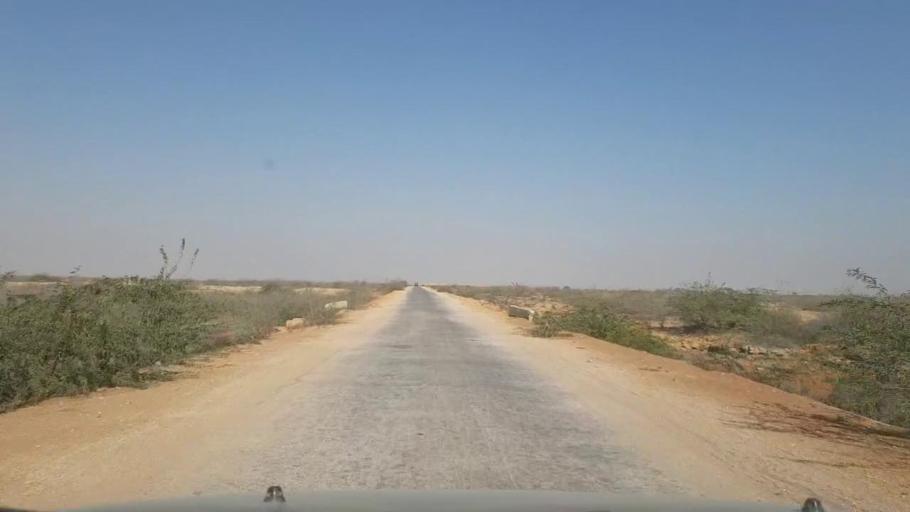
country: PK
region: Sindh
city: Thatta
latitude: 24.9448
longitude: 67.9520
